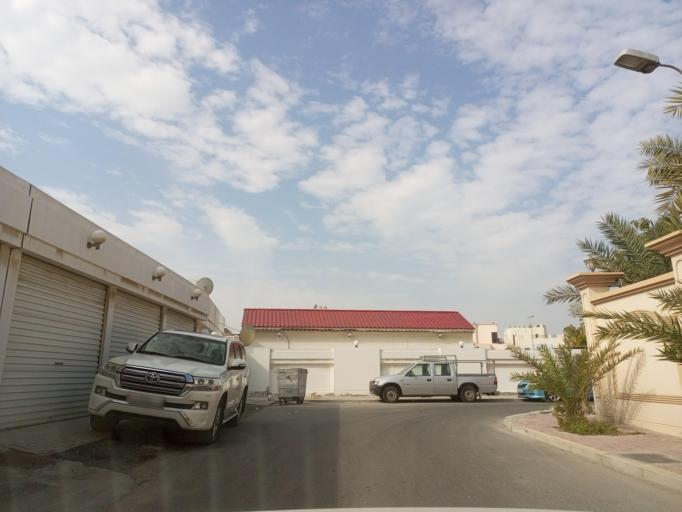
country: BH
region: Muharraq
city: Al Hadd
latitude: 26.2516
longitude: 50.6407
